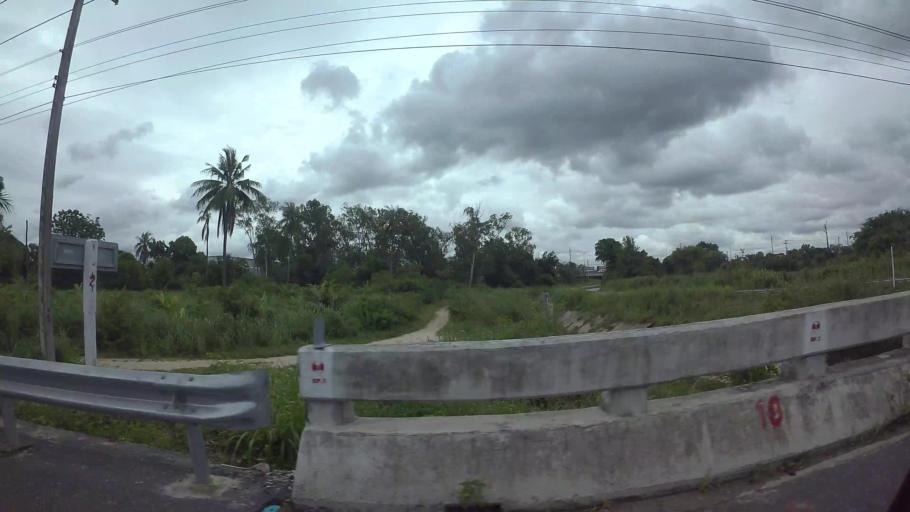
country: TH
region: Chon Buri
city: Si Racha
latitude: 13.1877
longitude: 100.9953
